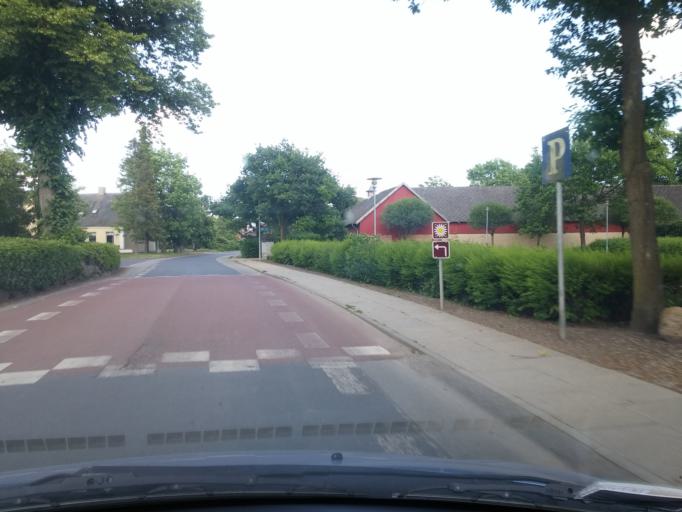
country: DK
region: South Denmark
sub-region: Kerteminde Kommune
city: Langeskov
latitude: 55.3811
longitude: 10.5667
